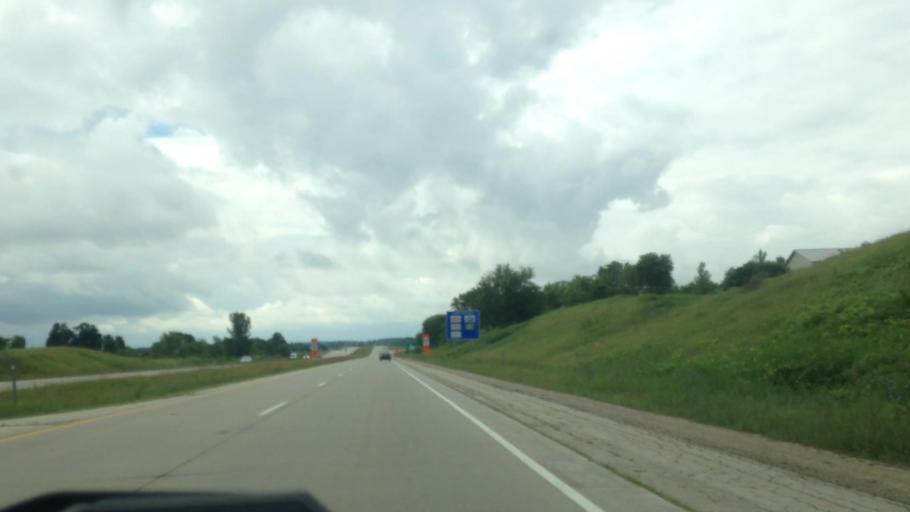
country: US
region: Wisconsin
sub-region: Washington County
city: Jackson
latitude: 43.3333
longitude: -88.1897
